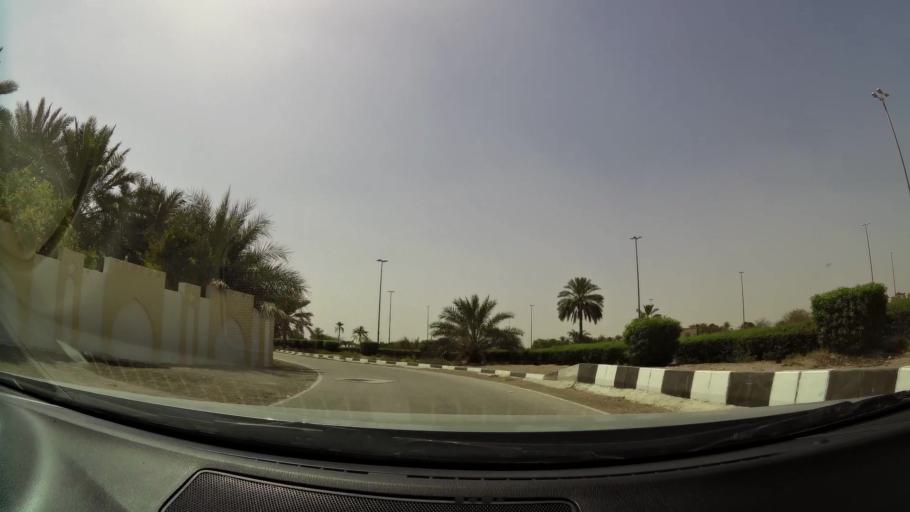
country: AE
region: Abu Dhabi
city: Al Ain
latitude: 24.2325
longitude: 55.7071
